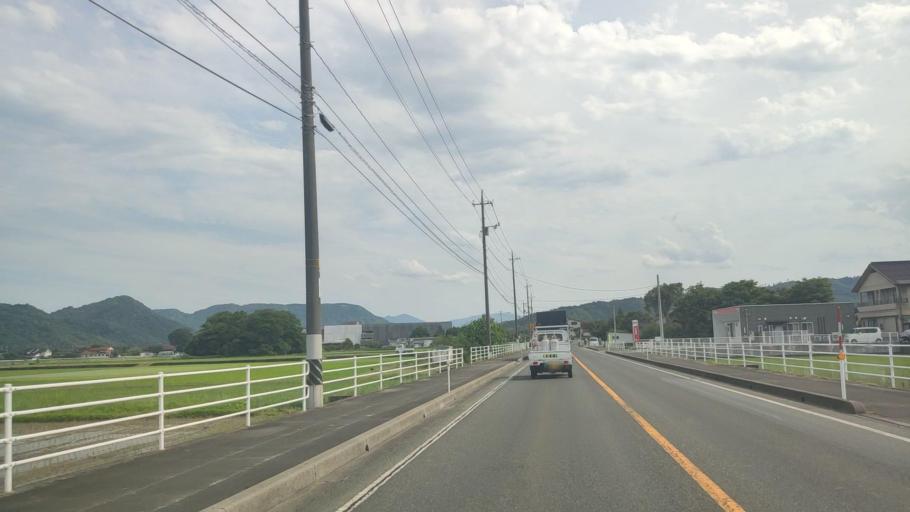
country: JP
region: Tottori
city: Tottori
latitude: 35.4580
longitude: 134.2034
